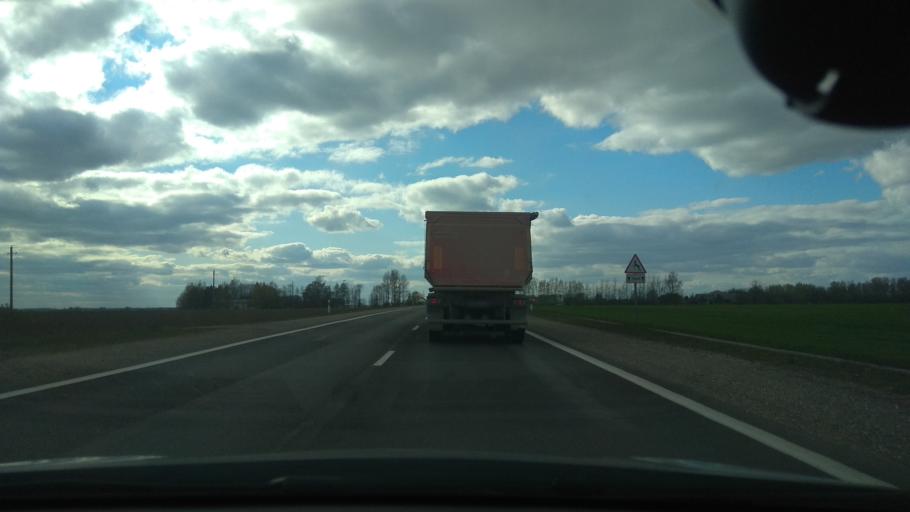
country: LT
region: Panevezys
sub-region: Panevezys City
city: Panevezys
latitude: 55.7361
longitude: 24.2091
